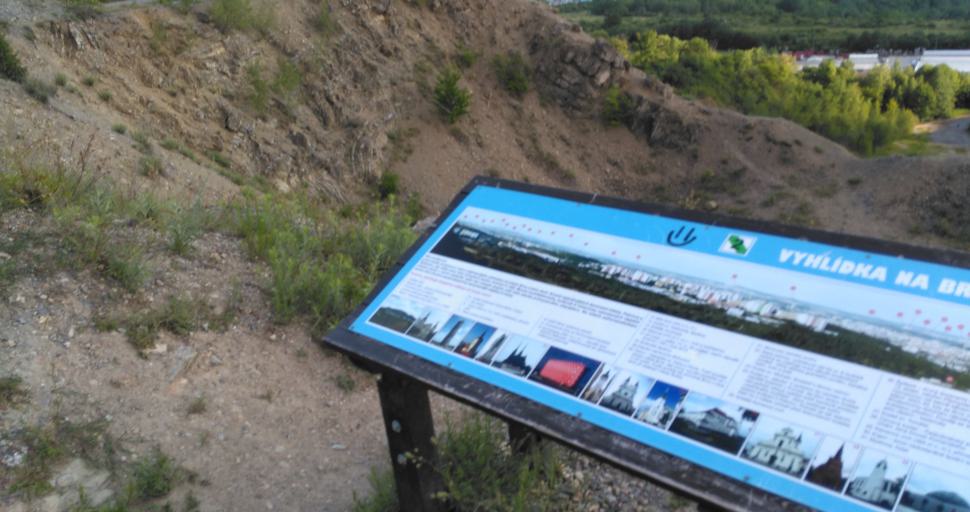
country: CZ
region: South Moravian
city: Bilovice nad Svitavou
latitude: 49.2186
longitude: 16.6739
